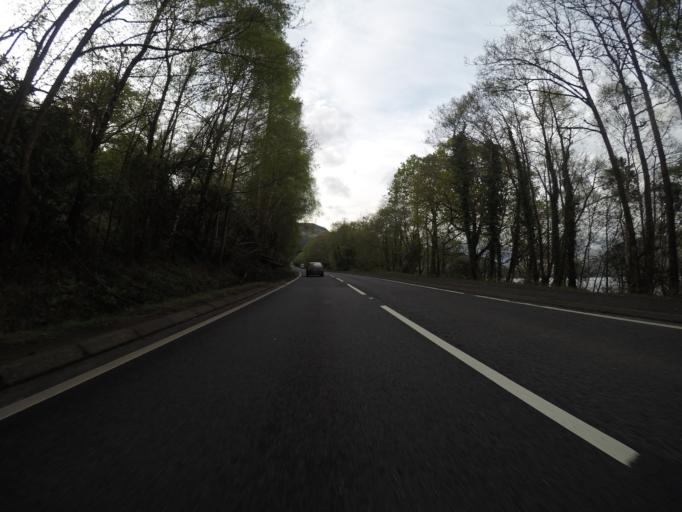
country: GB
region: Scotland
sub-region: Argyll and Bute
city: Garelochhead
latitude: 56.1969
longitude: -4.7039
